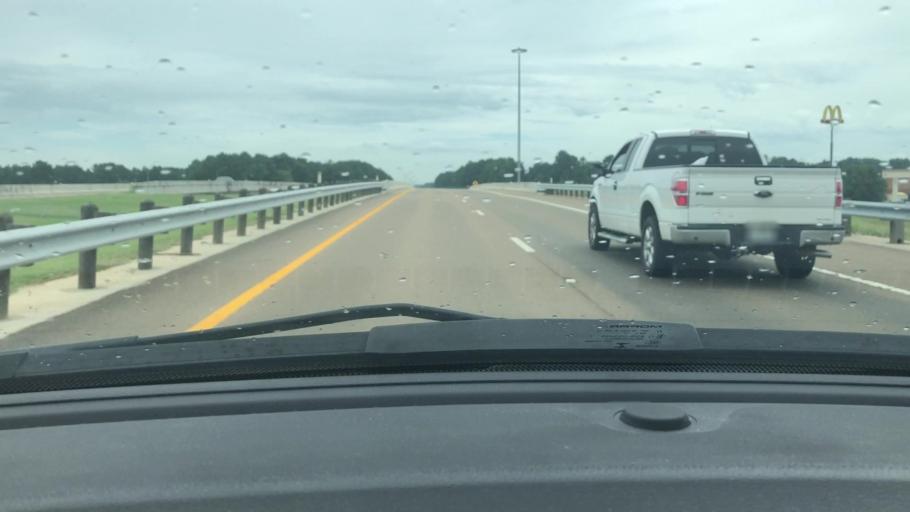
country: US
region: Texas
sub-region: Bowie County
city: Wake Village
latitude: 33.4197
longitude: -94.0965
